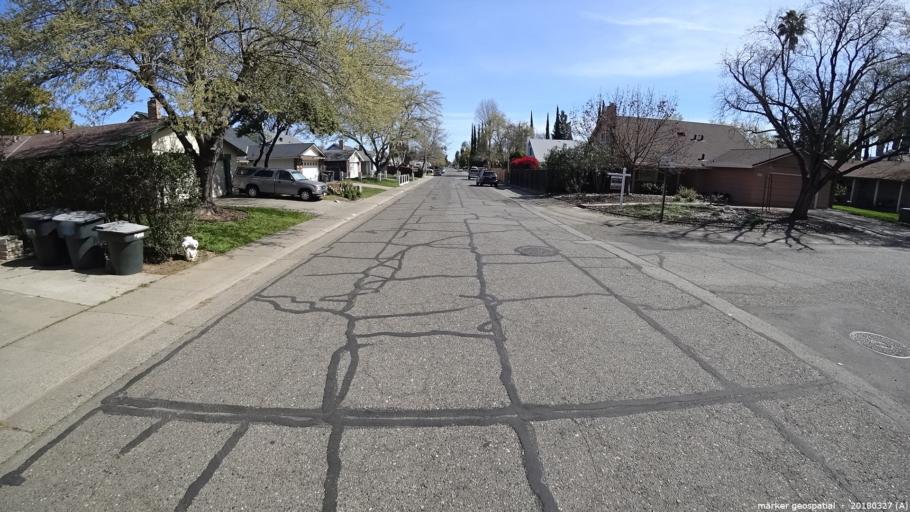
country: US
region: California
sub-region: Sacramento County
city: Rosemont
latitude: 38.5551
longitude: -121.3695
